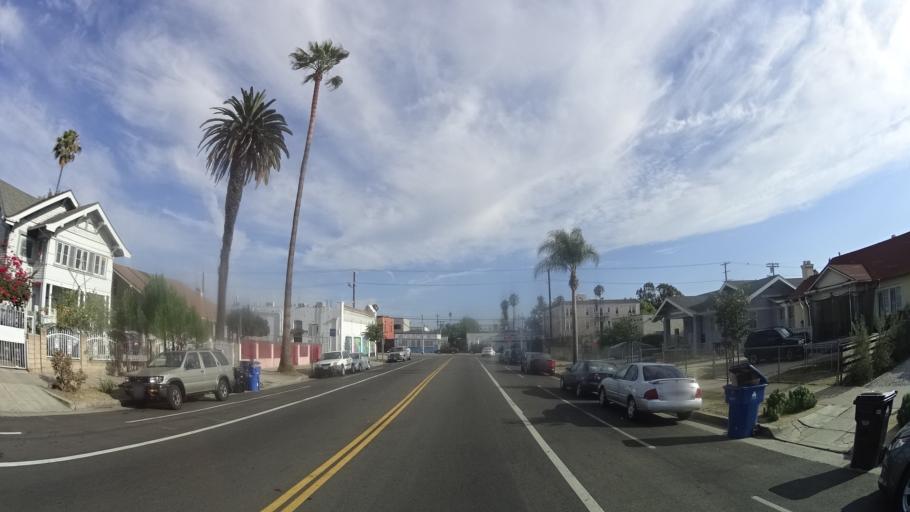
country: US
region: California
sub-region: Los Angeles County
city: Silver Lake
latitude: 34.0844
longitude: -118.2961
